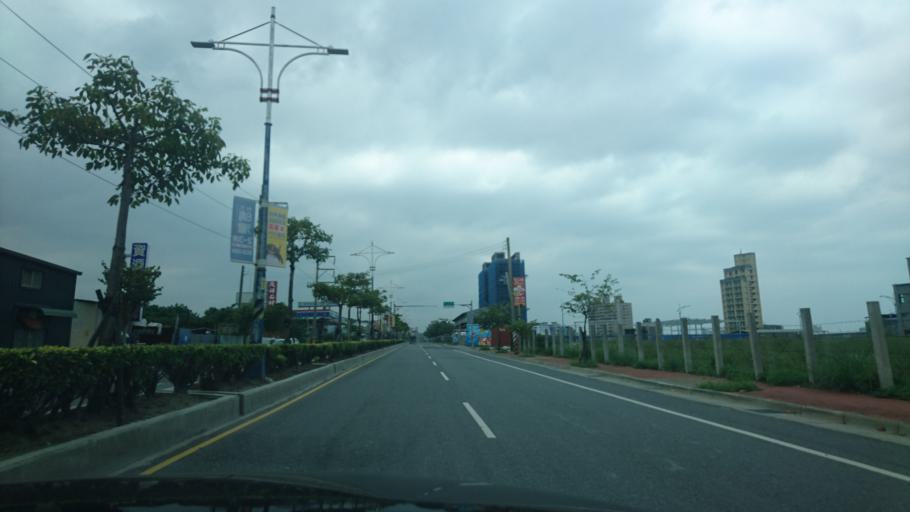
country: TW
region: Taipei
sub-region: Taipei
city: Banqiao
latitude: 25.1536
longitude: 121.4125
